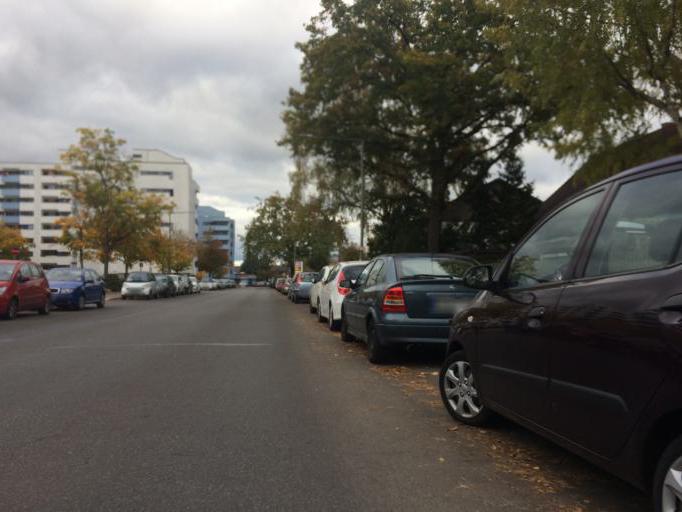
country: DE
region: Berlin
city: Wittenau
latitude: 52.5968
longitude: 13.3392
